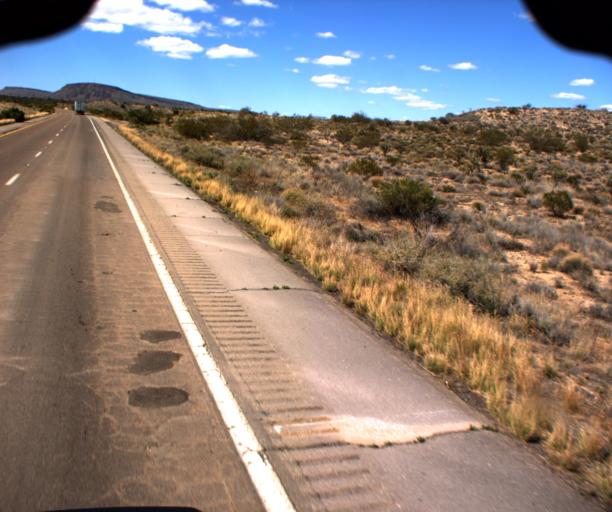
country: US
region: Arizona
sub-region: Mohave County
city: New Kingman-Butler
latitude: 35.1241
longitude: -113.6663
